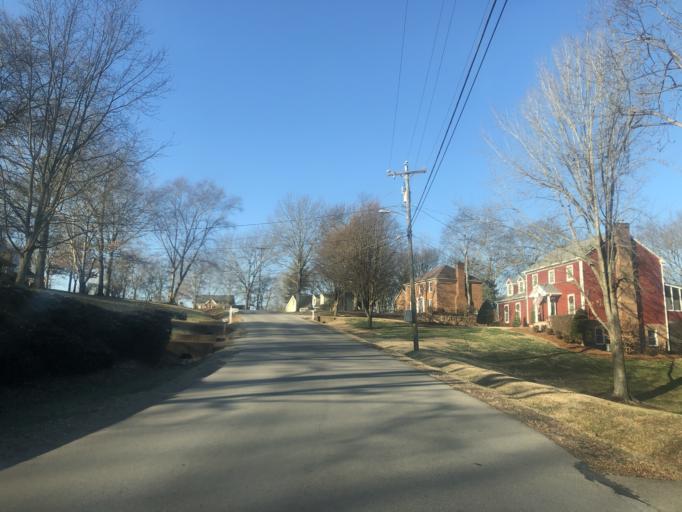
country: US
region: Tennessee
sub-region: Williamson County
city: Brentwood Estates
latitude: 36.0018
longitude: -86.7207
